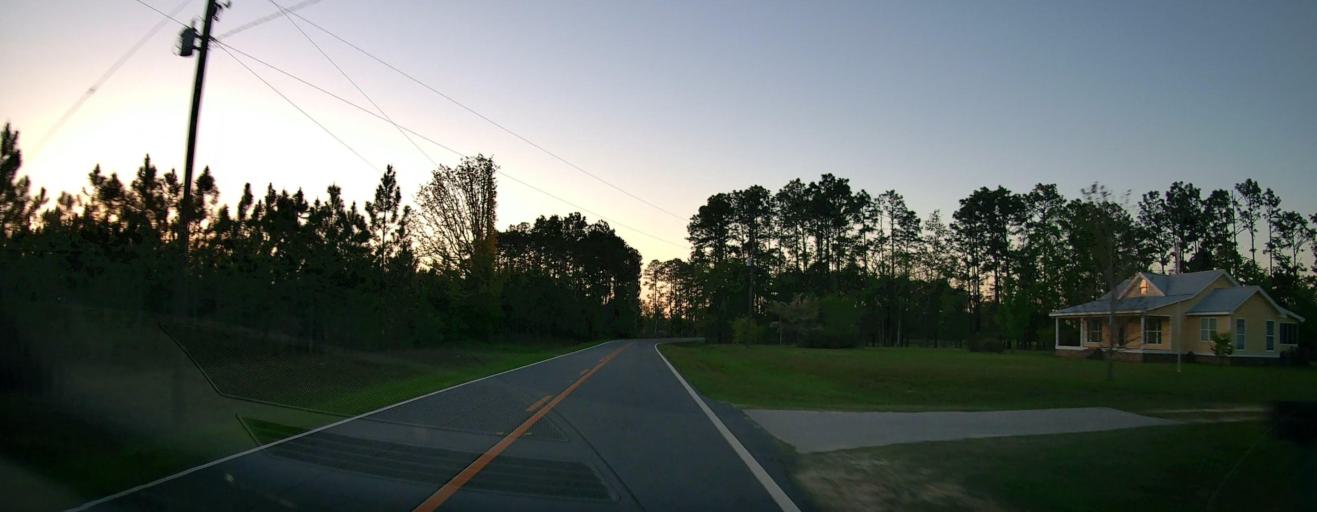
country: US
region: Georgia
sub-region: Wilcox County
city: Rochelle
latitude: 31.8079
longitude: -83.4597
